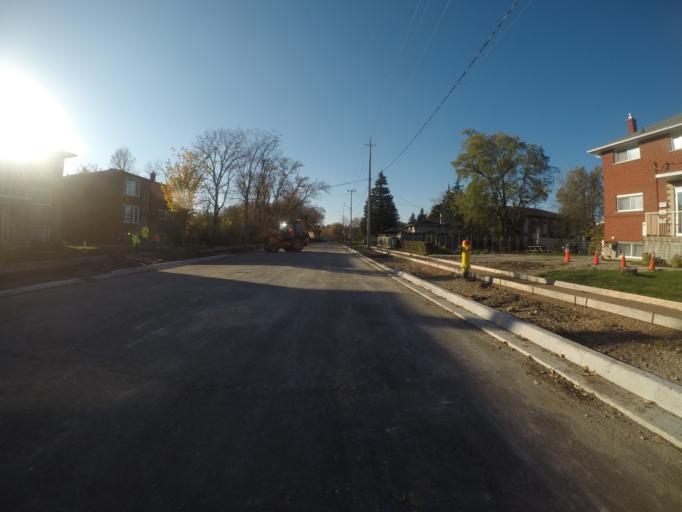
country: CA
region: Ontario
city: Kitchener
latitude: 43.4317
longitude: -80.4560
